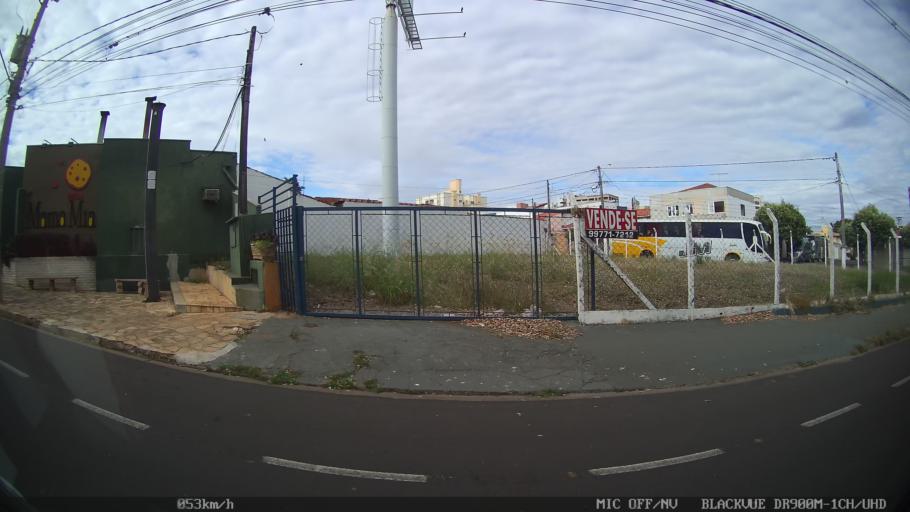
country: BR
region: Sao Paulo
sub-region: Sao Jose Do Rio Preto
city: Sao Jose do Rio Preto
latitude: -20.8242
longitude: -49.3981
